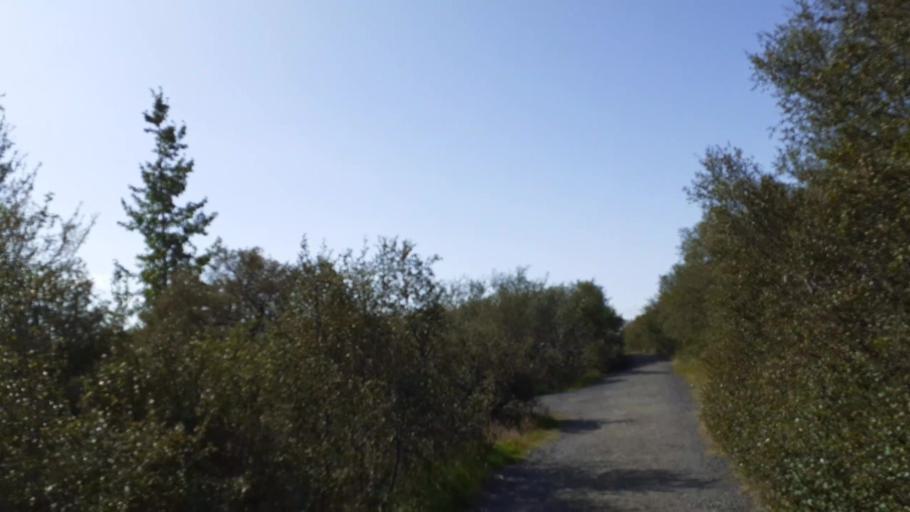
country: IS
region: West
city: Borgarnes
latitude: 64.7523
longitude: -21.5524
